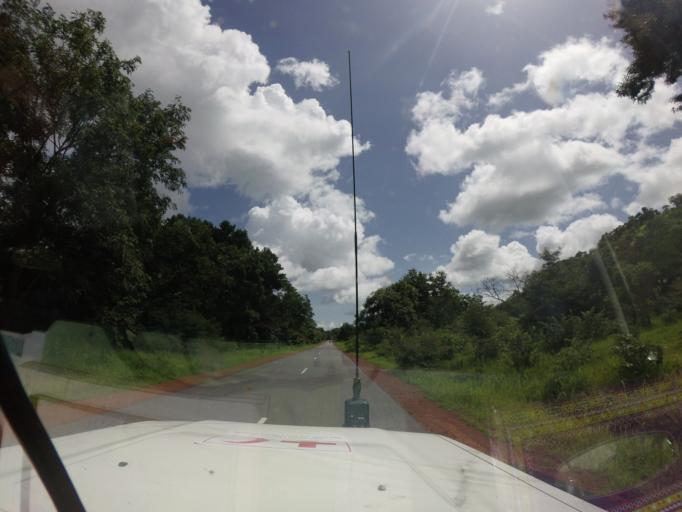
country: SL
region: Northern Province
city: Bindi
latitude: 10.1564
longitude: -11.6769
